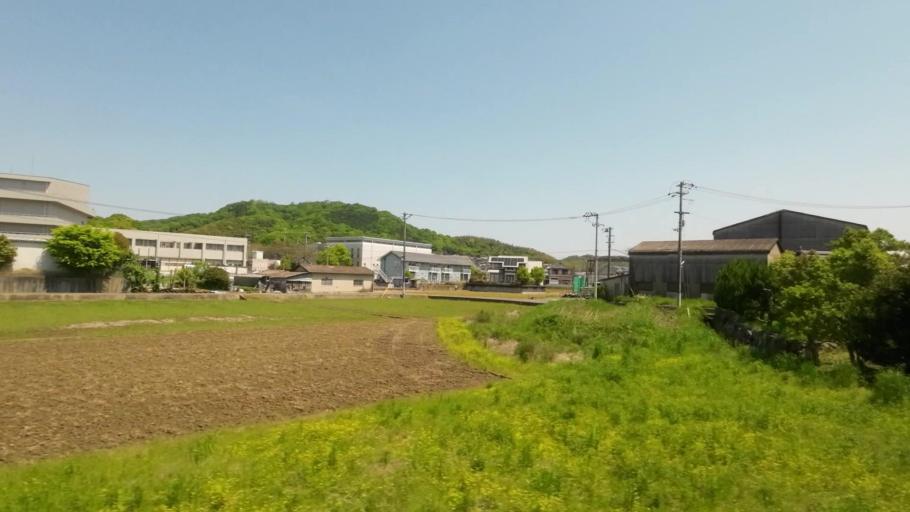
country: JP
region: Ehime
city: Hojo
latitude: 34.0967
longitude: 132.9526
